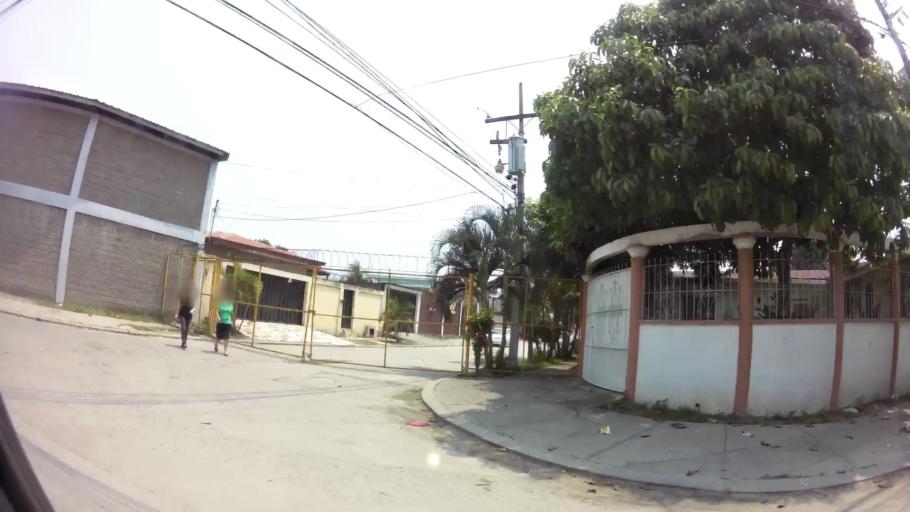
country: HN
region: Cortes
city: San Pedro Sula
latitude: 15.4916
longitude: -87.9967
